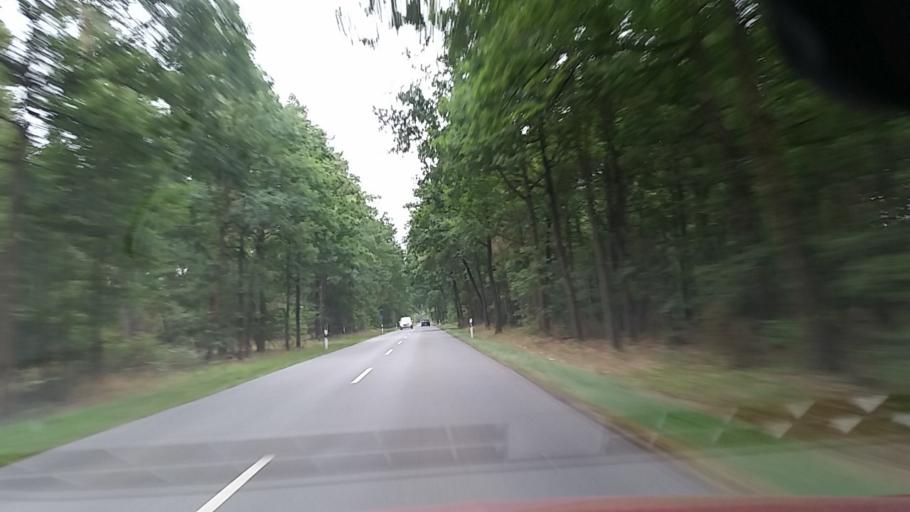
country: DE
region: Lower Saxony
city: Bokensdorf
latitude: 52.5152
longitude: 10.7162
